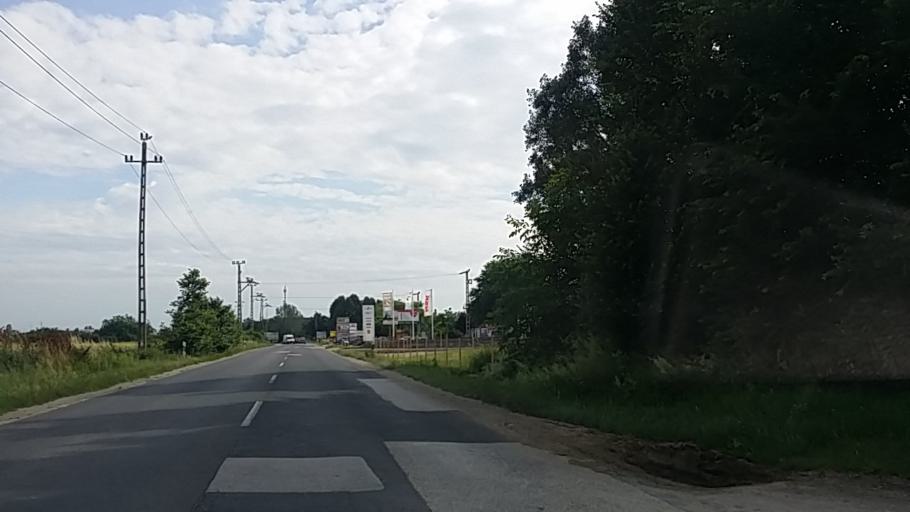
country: HU
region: Budapest
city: Budapest XXII. keruelet
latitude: 47.3859
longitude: 19.0503
